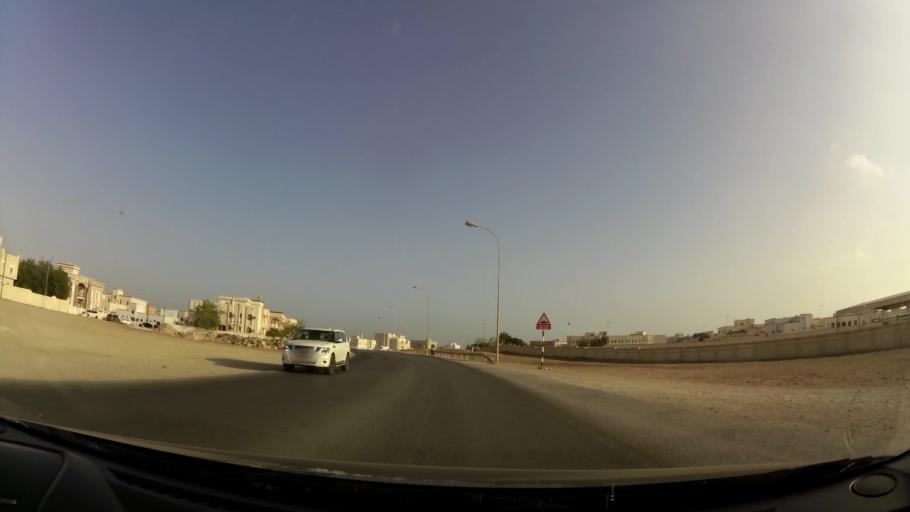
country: OM
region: Zufar
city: Salalah
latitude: 17.0101
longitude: 54.0333
